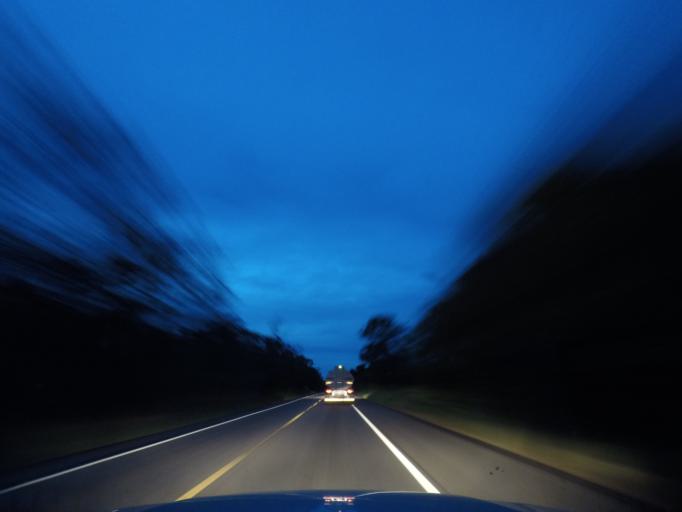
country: BR
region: Bahia
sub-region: Andarai
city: Vera Cruz
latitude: -12.4876
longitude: -41.3423
